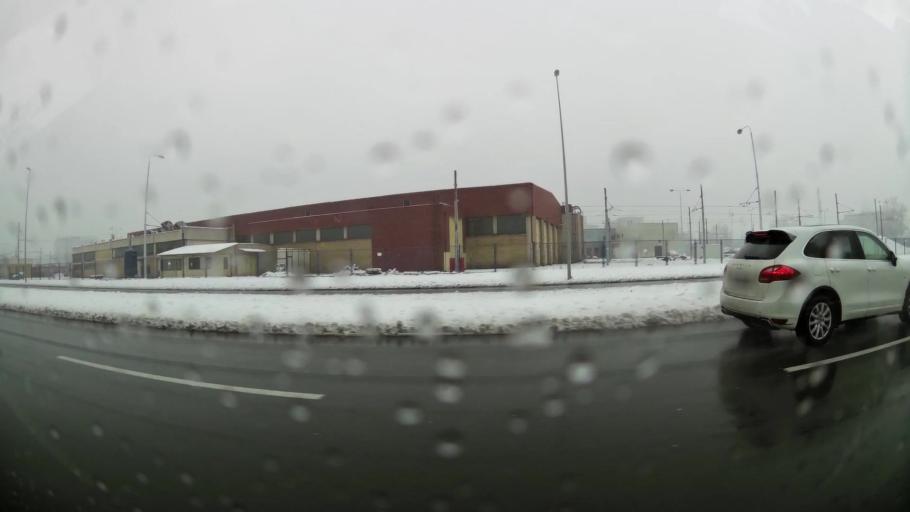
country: RS
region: Central Serbia
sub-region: Belgrade
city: Novi Beograd
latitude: 44.8101
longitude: 20.4098
